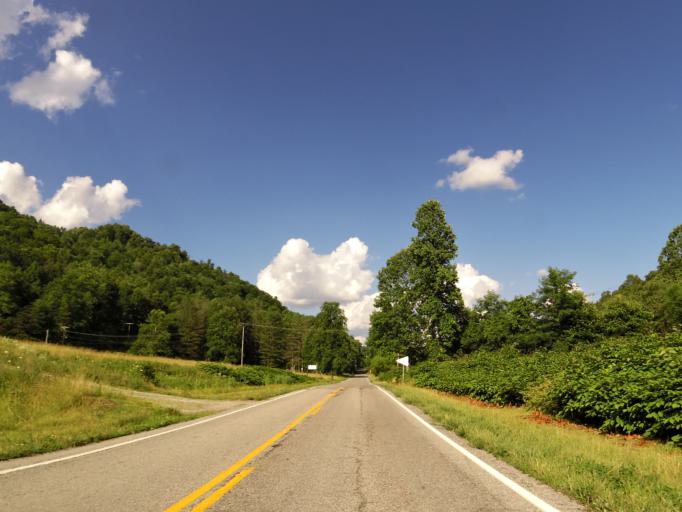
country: US
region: Virginia
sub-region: Lee County
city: Jonesville
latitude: 36.7632
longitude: -83.1824
